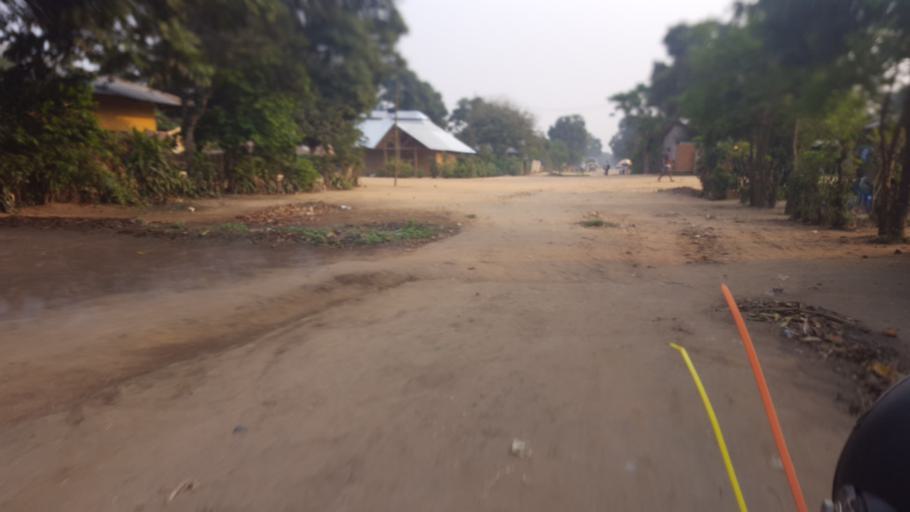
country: CD
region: Bandundu
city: Bandundu
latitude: -3.3201
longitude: 17.3787
